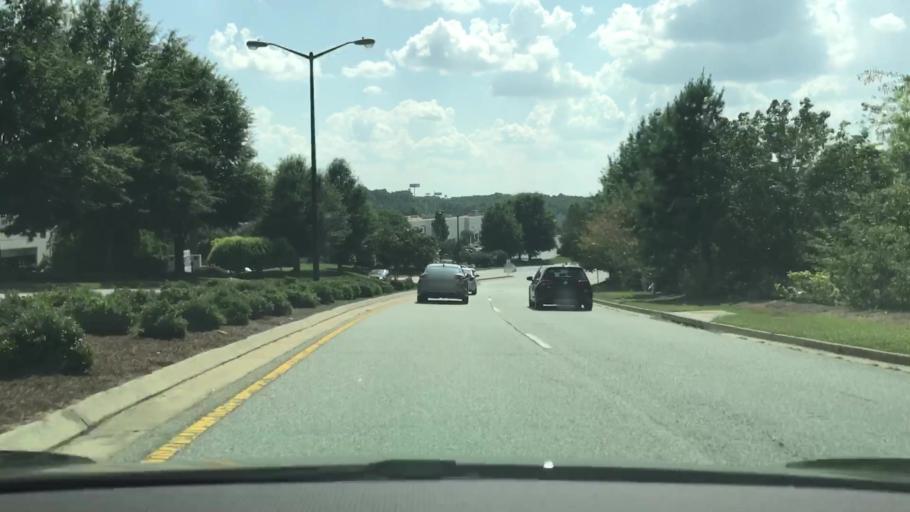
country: US
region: Georgia
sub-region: Gwinnett County
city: Suwanee
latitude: 34.0408
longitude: -84.0384
